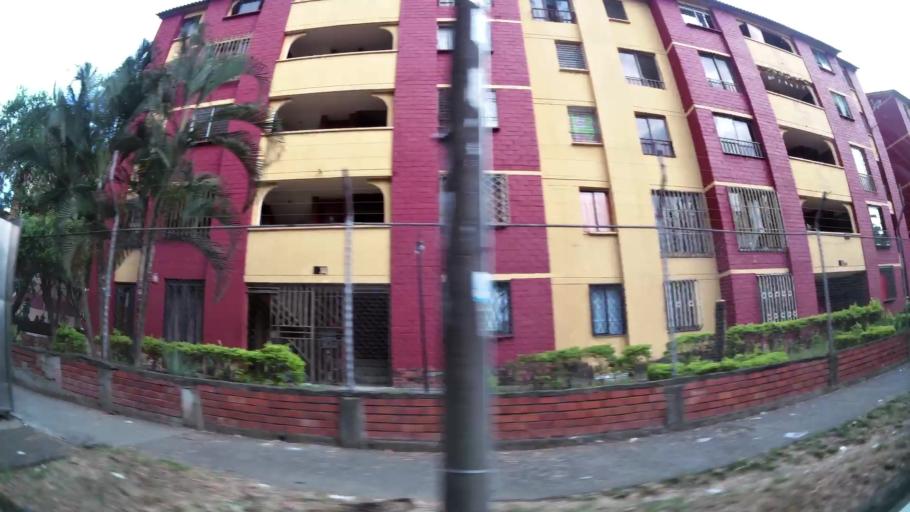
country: CO
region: Valle del Cauca
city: Cali
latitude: 3.4752
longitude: -76.4919
